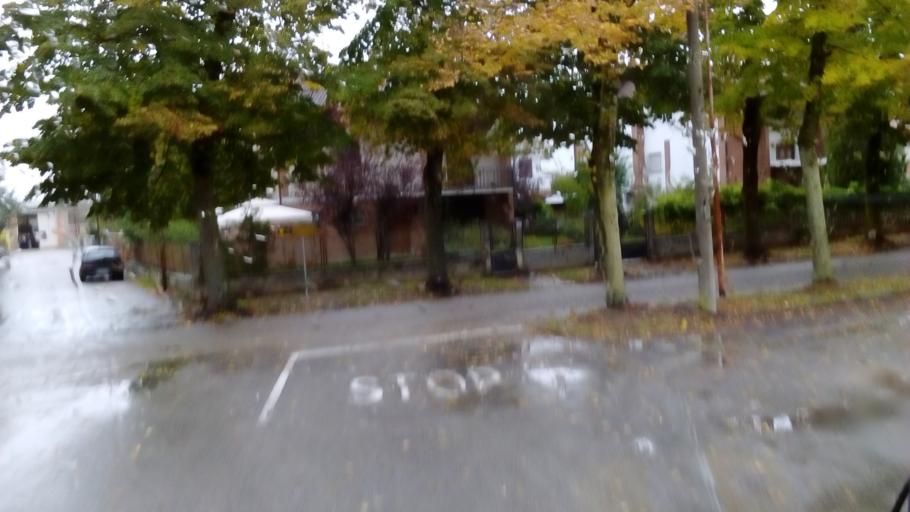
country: IT
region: Emilia-Romagna
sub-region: Provincia di Reggio Emilia
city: Luzzara
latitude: 44.9565
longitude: 10.6935
